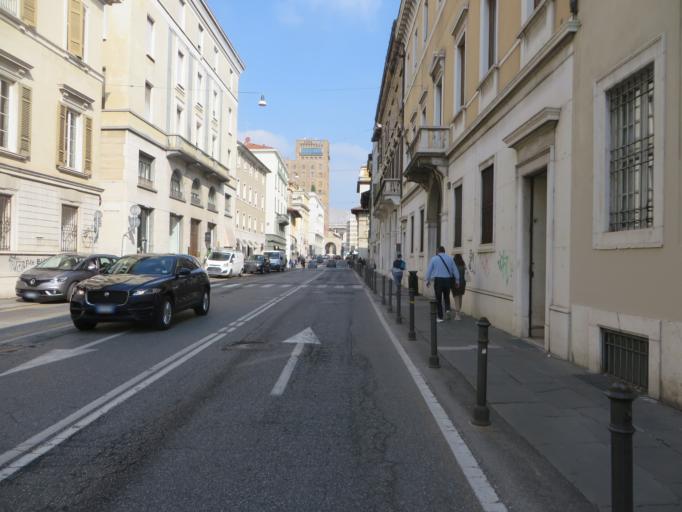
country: IT
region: Lombardy
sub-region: Provincia di Brescia
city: Brescia
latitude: 45.5363
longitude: 10.2188
